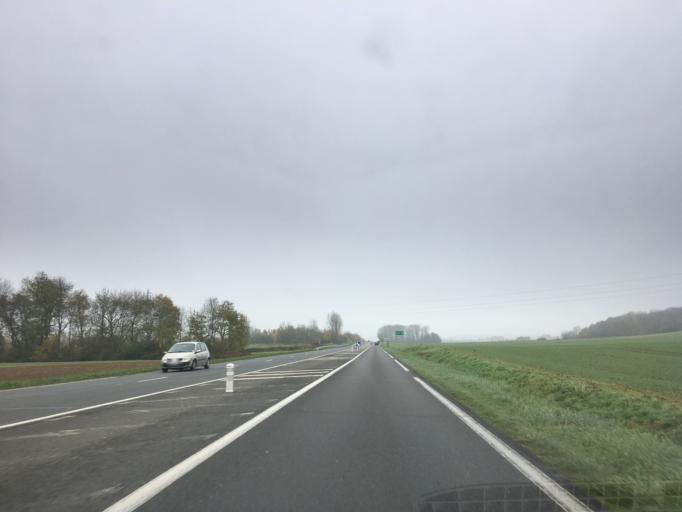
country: FR
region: Ile-de-France
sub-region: Departement de Seine-et-Marne
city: La Grande-Paroisse
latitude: 48.3614
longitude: 2.8823
